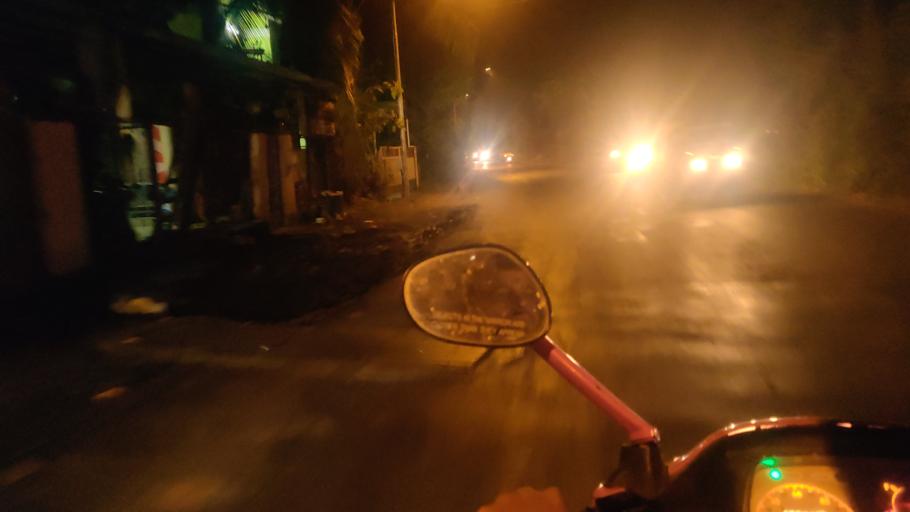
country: IN
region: Maharashtra
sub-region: Thane
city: Bhayandar
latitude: 19.2995
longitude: 72.8327
